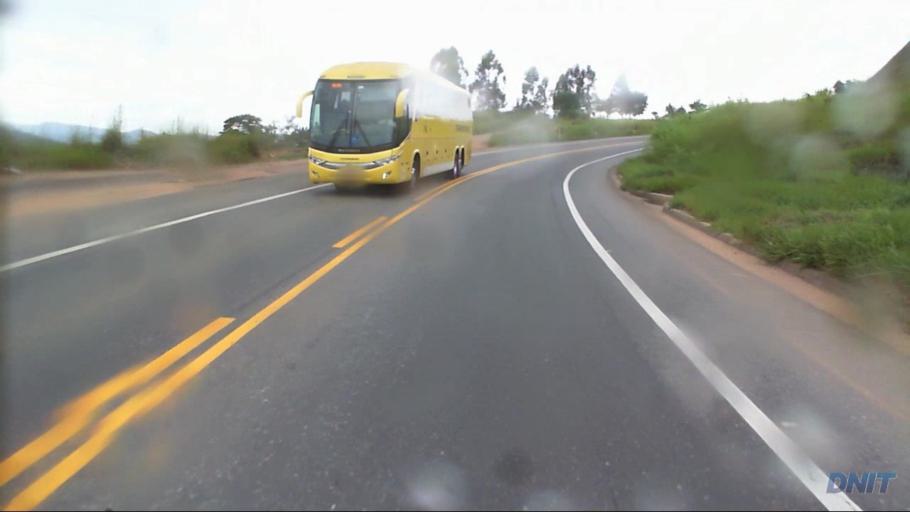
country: BR
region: Minas Gerais
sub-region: Nova Era
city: Nova Era
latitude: -19.6843
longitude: -42.9822
